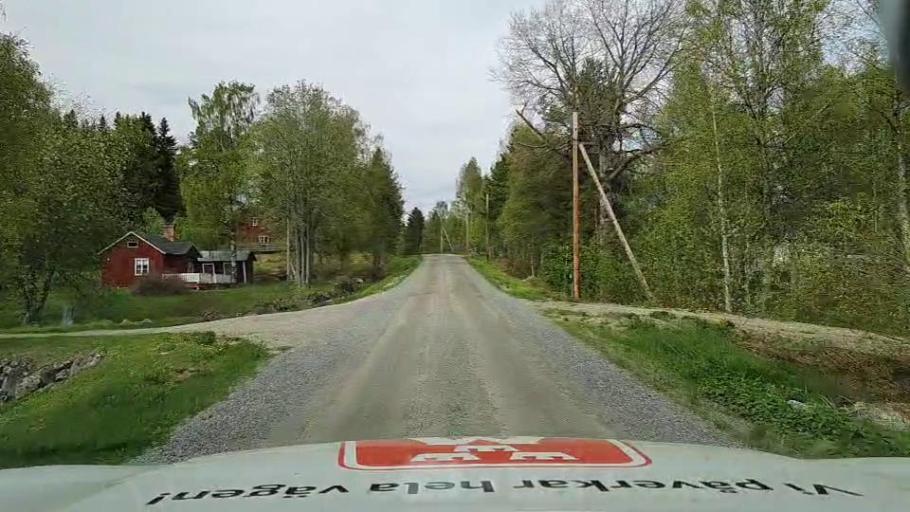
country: SE
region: Jaemtland
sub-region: OEstersunds Kommun
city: Brunflo
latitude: 62.6129
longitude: 14.9453
